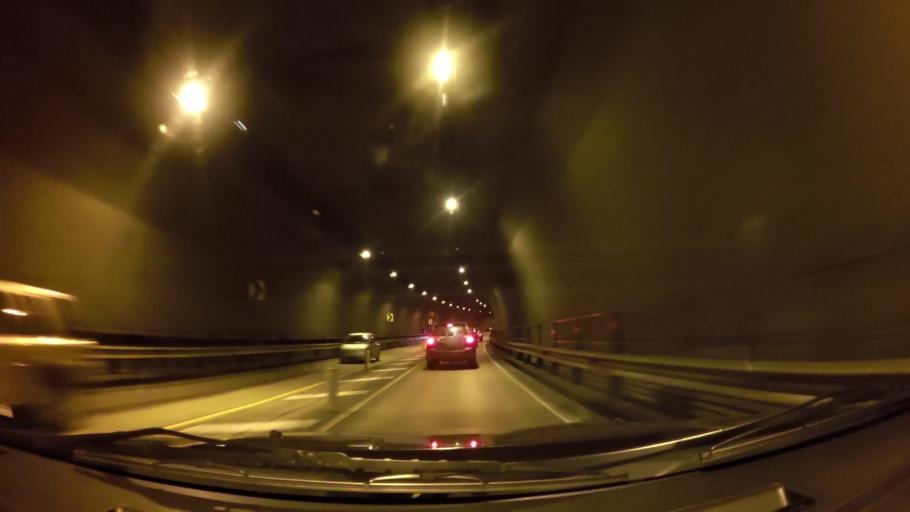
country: EC
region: Pichincha
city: Quito
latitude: -0.1922
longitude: -78.4705
